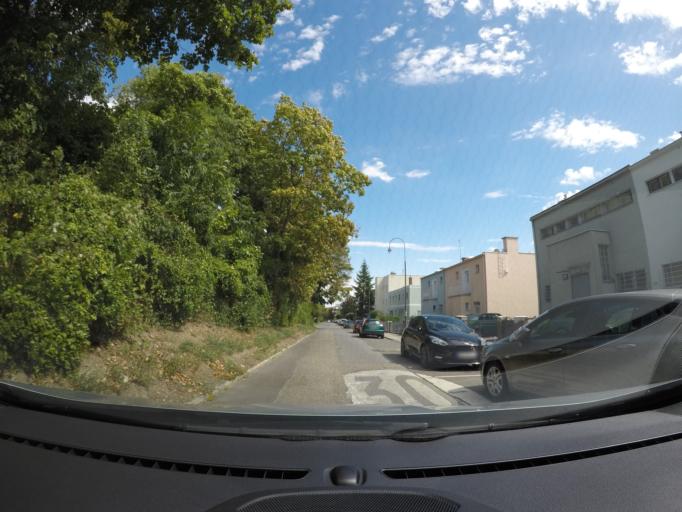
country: AT
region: Lower Austria
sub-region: Politischer Bezirk Modling
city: Perchtoldsdorf
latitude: 48.1808
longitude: 16.2680
